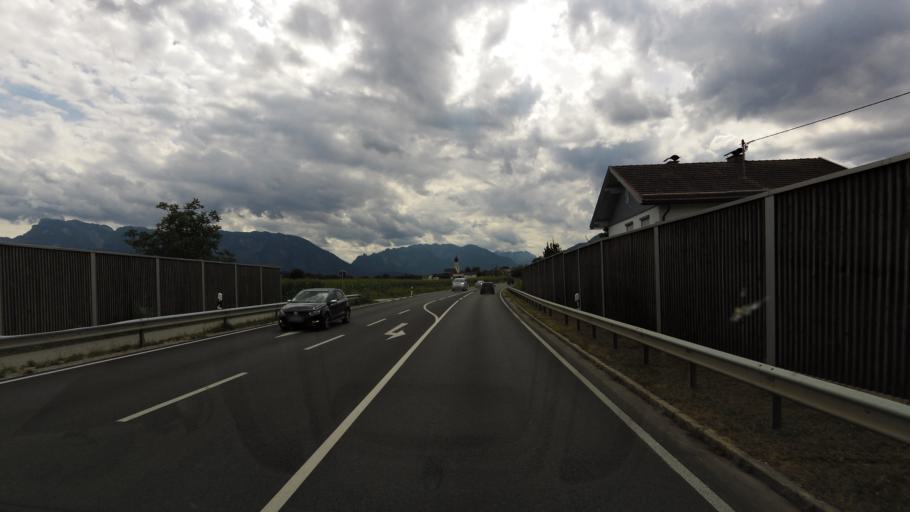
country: DE
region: Bavaria
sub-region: Upper Bavaria
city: Ainring
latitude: 47.8119
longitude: 12.9651
